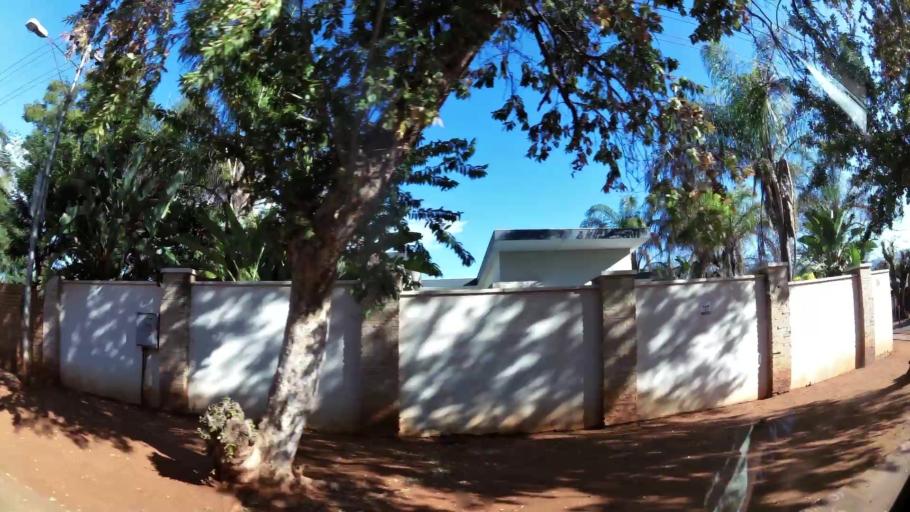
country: ZA
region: Limpopo
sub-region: Waterberg District Municipality
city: Mokopane
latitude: -24.1776
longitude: 28.9965
